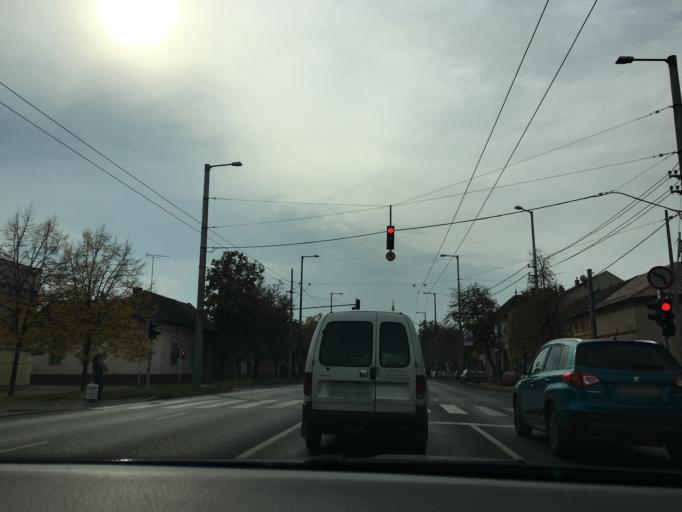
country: HU
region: Hajdu-Bihar
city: Debrecen
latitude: 47.5411
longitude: 21.6405
